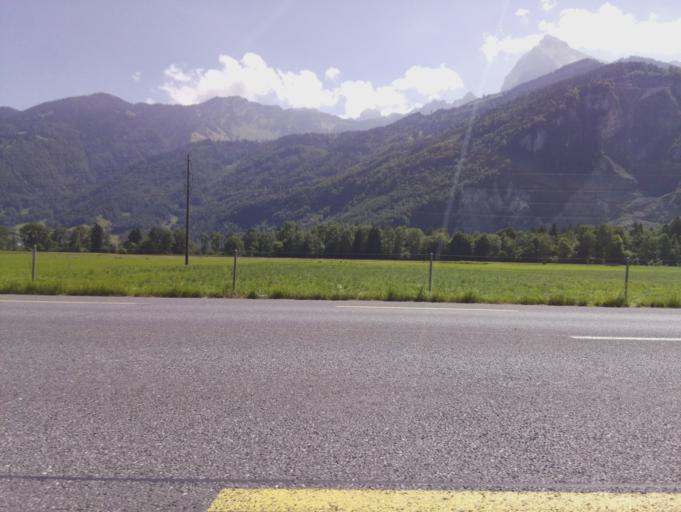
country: CH
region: Glarus
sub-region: Glarus
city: Netstal
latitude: 47.0799
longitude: 9.0554
